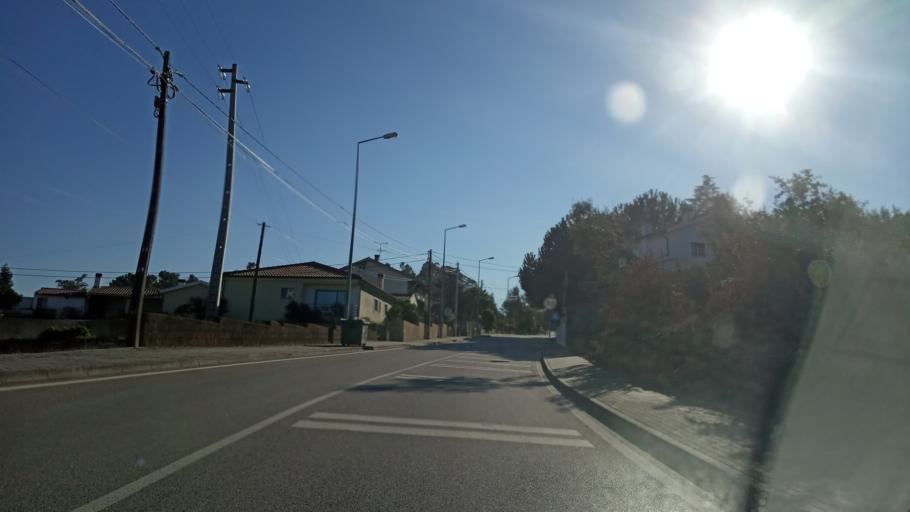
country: PT
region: Aveiro
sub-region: Anadia
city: Anadia
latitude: 40.4314
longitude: -8.4334
